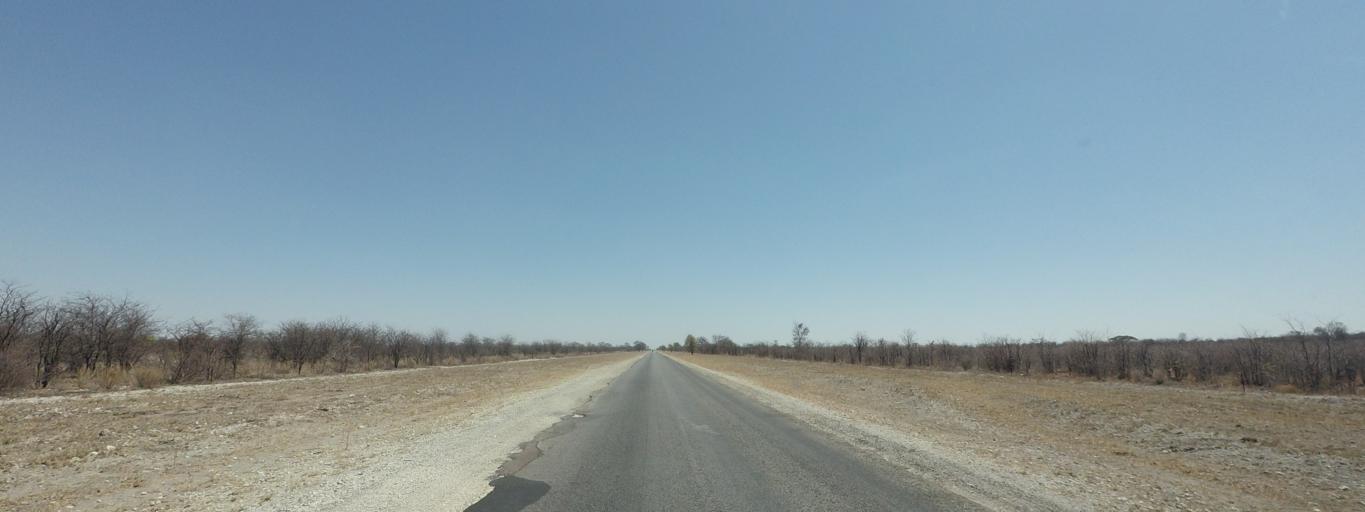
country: BW
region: Central
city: Nata
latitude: -20.3660
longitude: 26.3201
